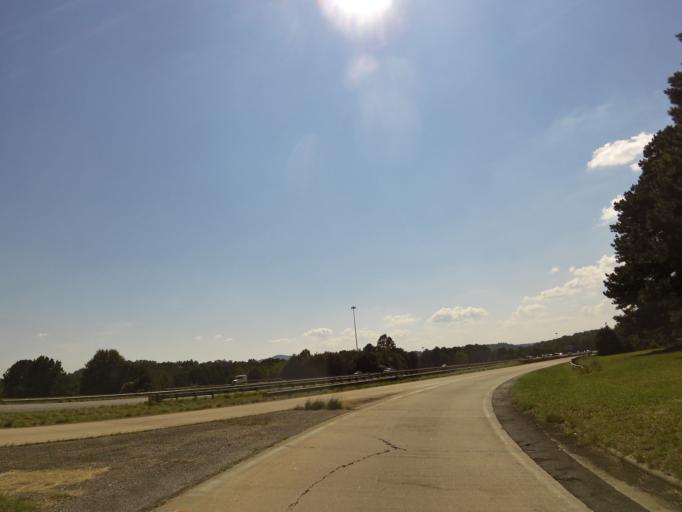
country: US
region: North Carolina
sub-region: Catawba County
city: Hickory
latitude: 35.7090
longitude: -81.3518
